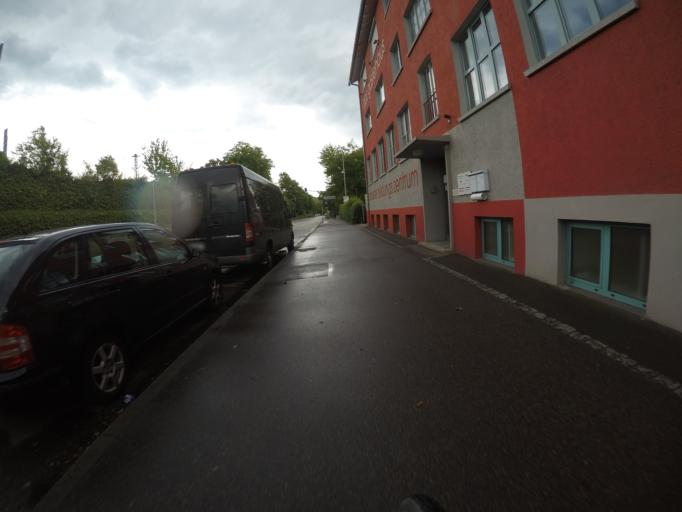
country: DE
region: Baden-Wuerttemberg
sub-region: Regierungsbezirk Stuttgart
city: Fellbach
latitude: 48.7773
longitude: 9.2531
